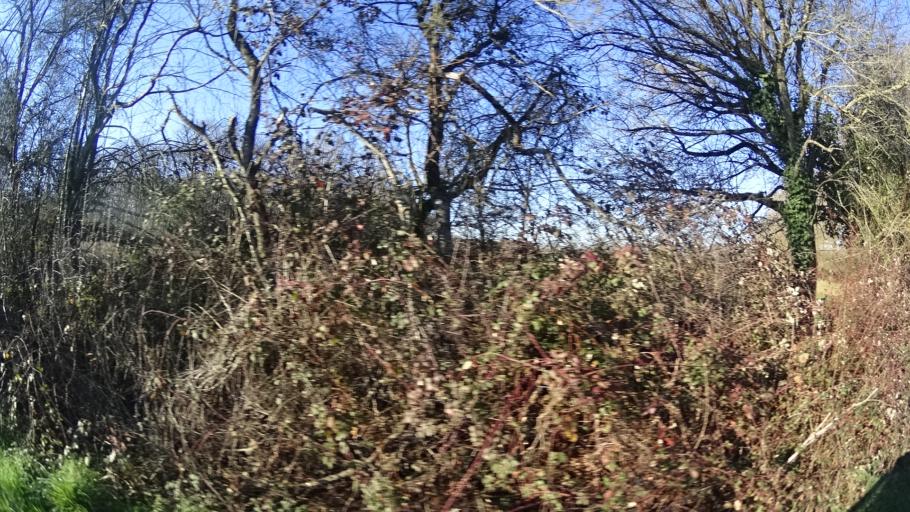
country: FR
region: Brittany
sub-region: Departement du Morbihan
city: Allaire
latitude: 47.6448
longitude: -2.1499
